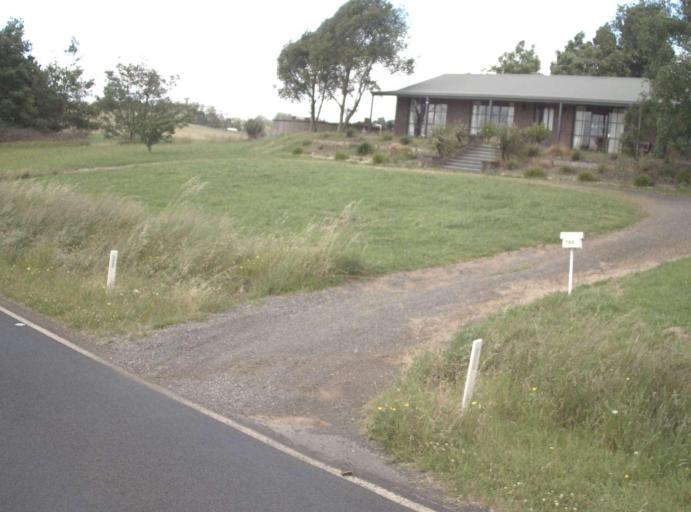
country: AU
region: Victoria
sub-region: Baw Baw
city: Warragul
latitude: -38.0884
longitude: 145.9201
